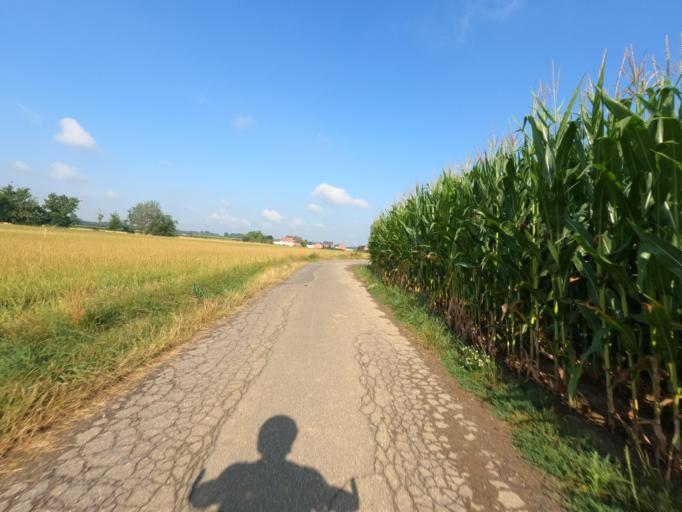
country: DE
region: North Rhine-Westphalia
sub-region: Regierungsbezirk Koln
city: Heinsberg
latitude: 51.0898
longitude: 6.0950
